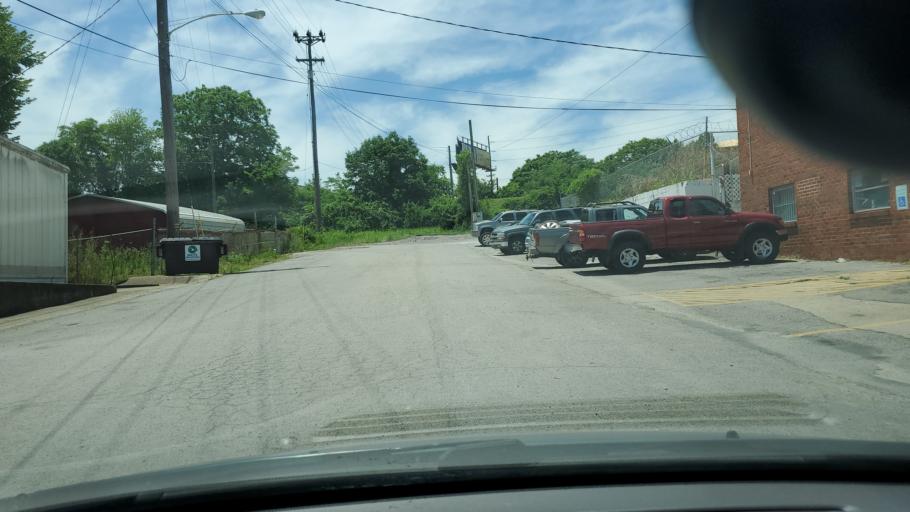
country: US
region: Tennessee
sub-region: Davidson County
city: Nashville
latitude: 36.2071
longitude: -86.7485
